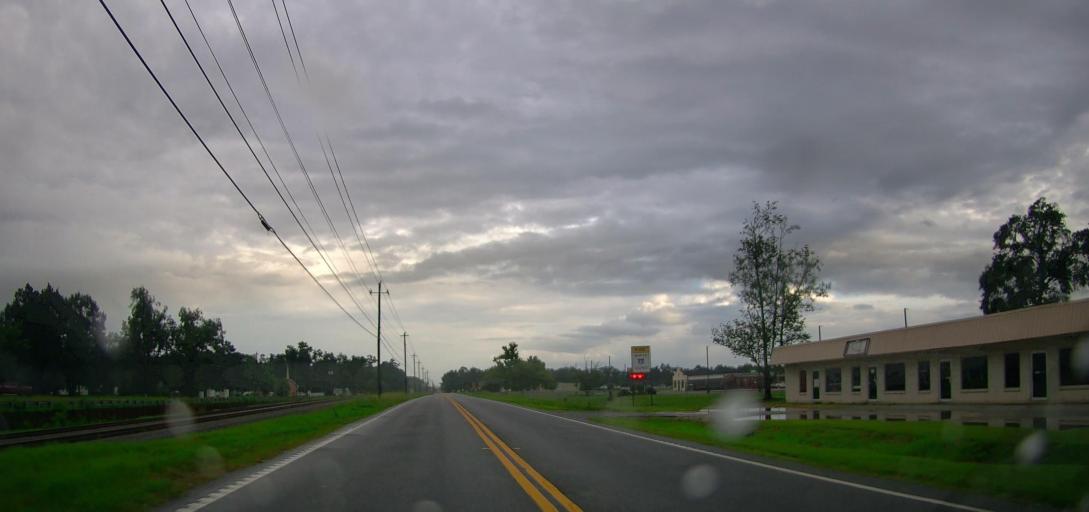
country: US
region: Georgia
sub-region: Ware County
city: Deenwood
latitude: 31.2515
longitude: -82.3761
